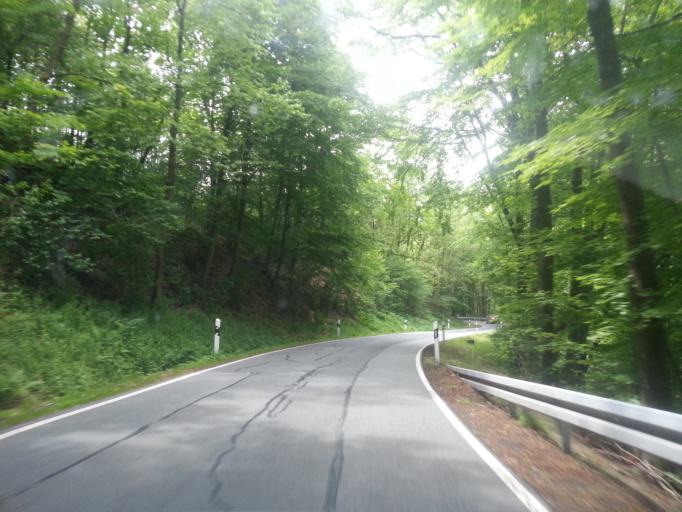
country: DE
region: Hesse
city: Lutzelbach
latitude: 49.7274
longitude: 8.7043
